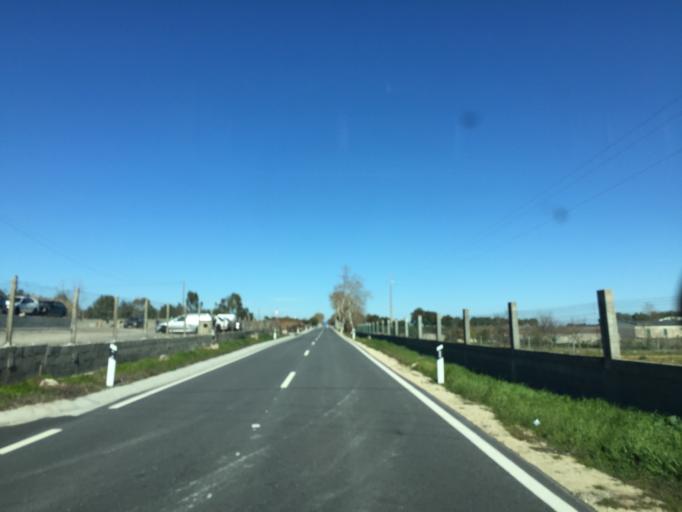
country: PT
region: Guarda
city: Alcains
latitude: 39.9398
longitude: -7.4573
